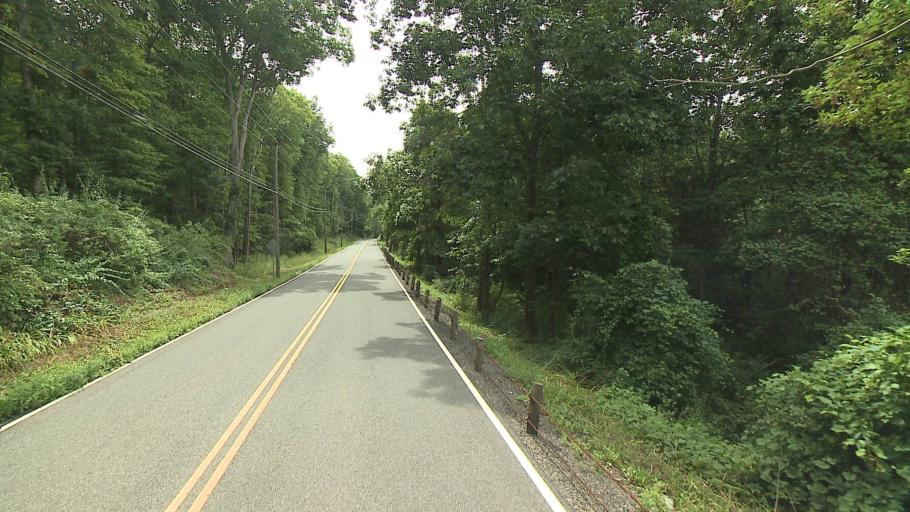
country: US
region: Connecticut
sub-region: Litchfield County
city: New Milford
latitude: 41.5839
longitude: -73.3219
